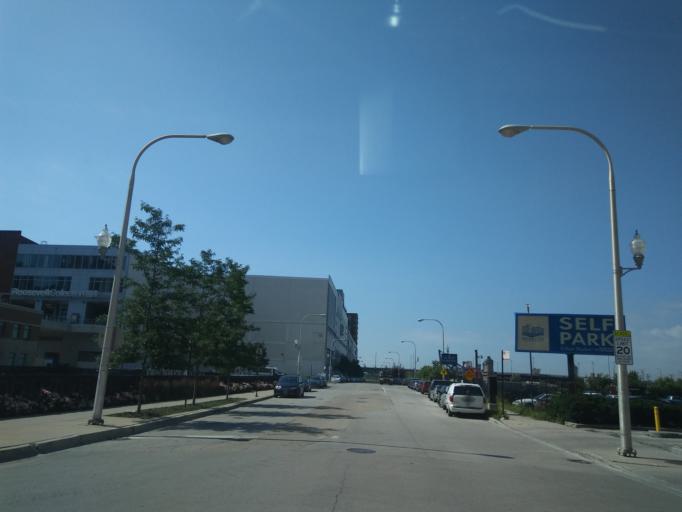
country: US
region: Illinois
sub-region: Cook County
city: Chicago
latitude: 41.8707
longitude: -87.6335
